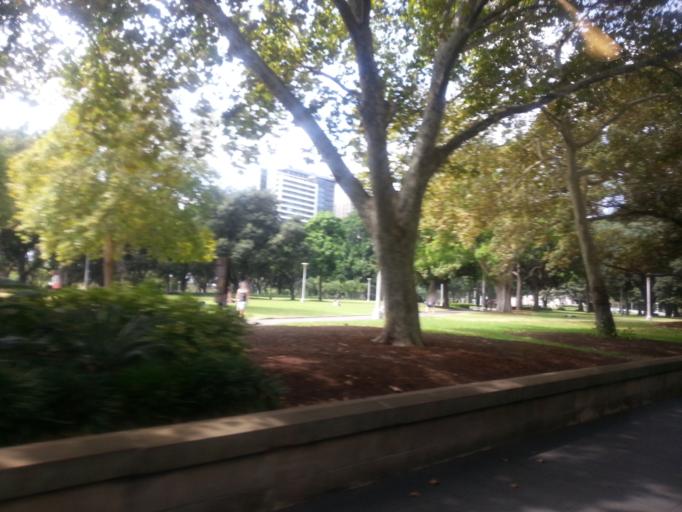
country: AU
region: New South Wales
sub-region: City of Sydney
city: Sydney
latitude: -33.8735
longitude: 151.2103
